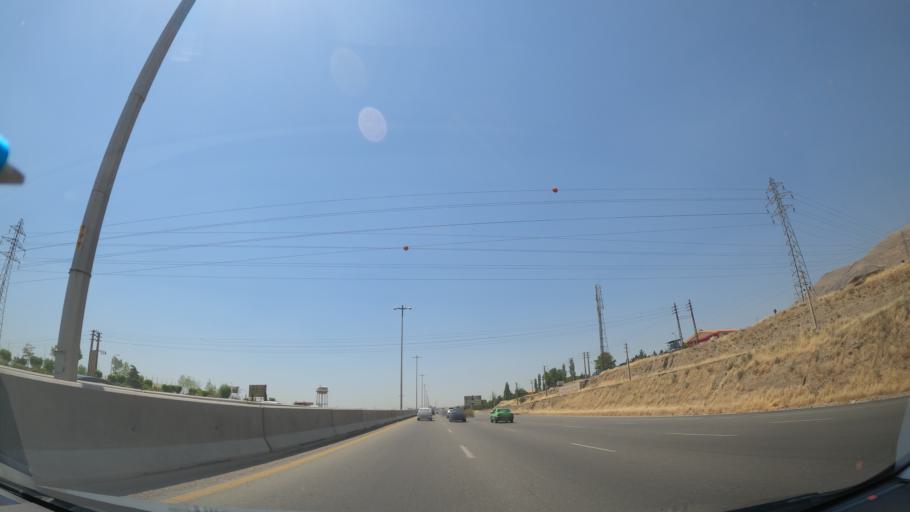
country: IR
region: Tehran
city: Shahr-e Qods
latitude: 35.7603
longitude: 51.0648
